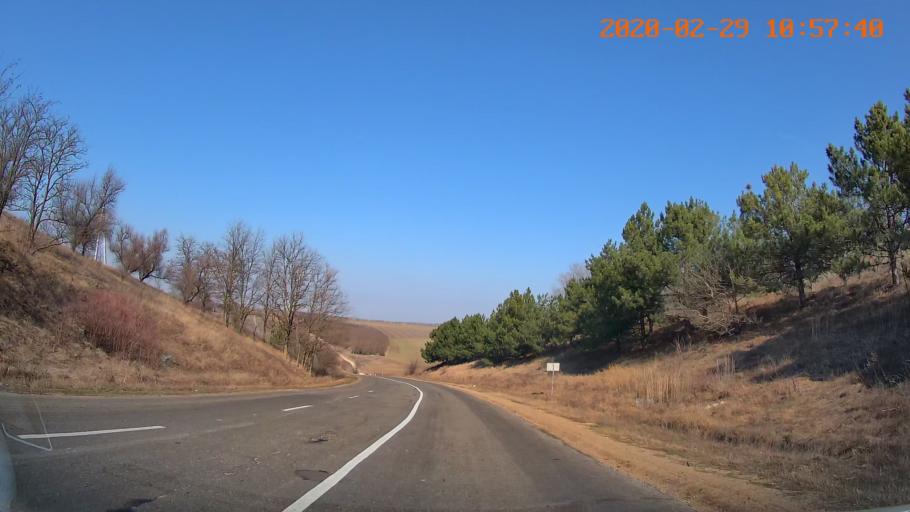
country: MD
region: Telenesti
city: Grigoriopol
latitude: 47.1620
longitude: 29.3216
